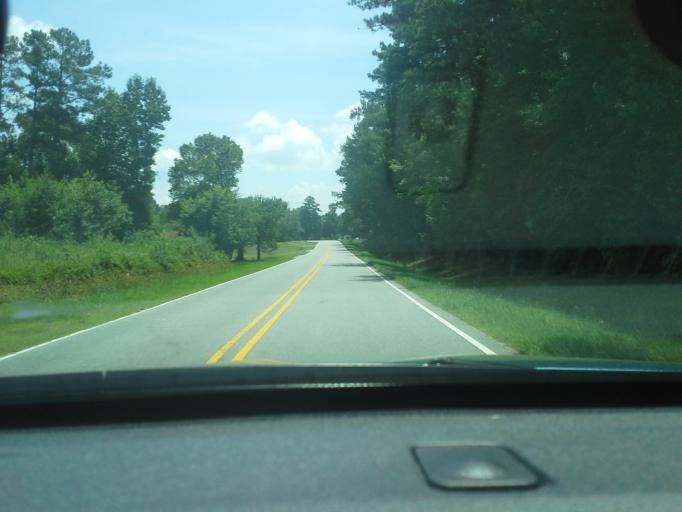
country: US
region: North Carolina
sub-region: Chowan County
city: Edenton
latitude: 35.9280
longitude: -76.6025
